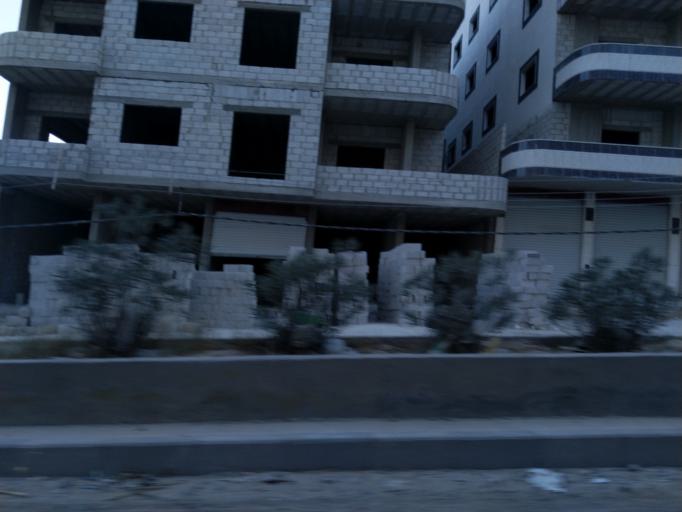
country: SY
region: Rif-dimashq
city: At Tall
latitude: 33.5727
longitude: 36.3052
